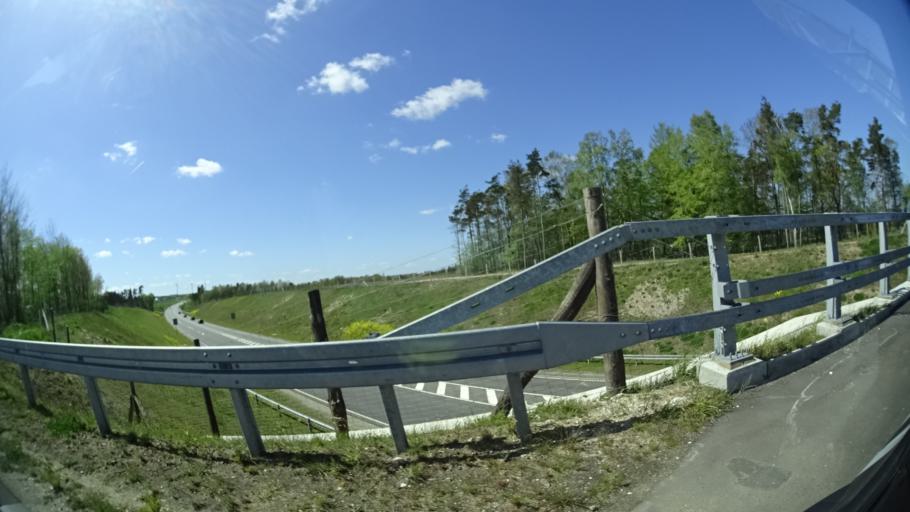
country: DK
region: Central Jutland
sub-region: Randers Kommune
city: Assentoft
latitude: 56.4172
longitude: 10.0934
